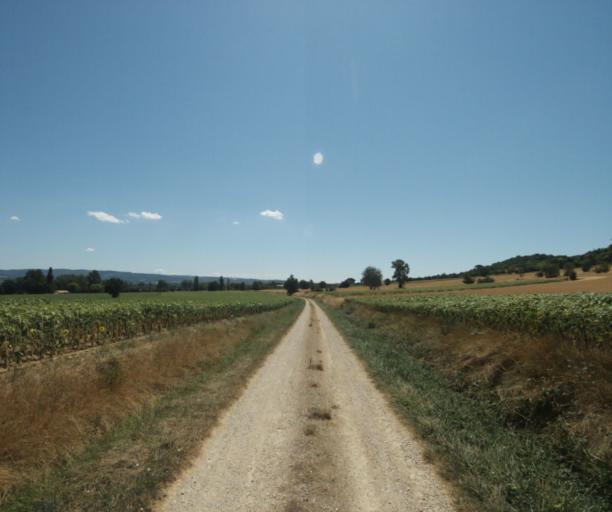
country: FR
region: Midi-Pyrenees
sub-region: Departement de la Haute-Garonne
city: Saint-Felix-Lauragais
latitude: 43.4698
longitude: 1.9235
